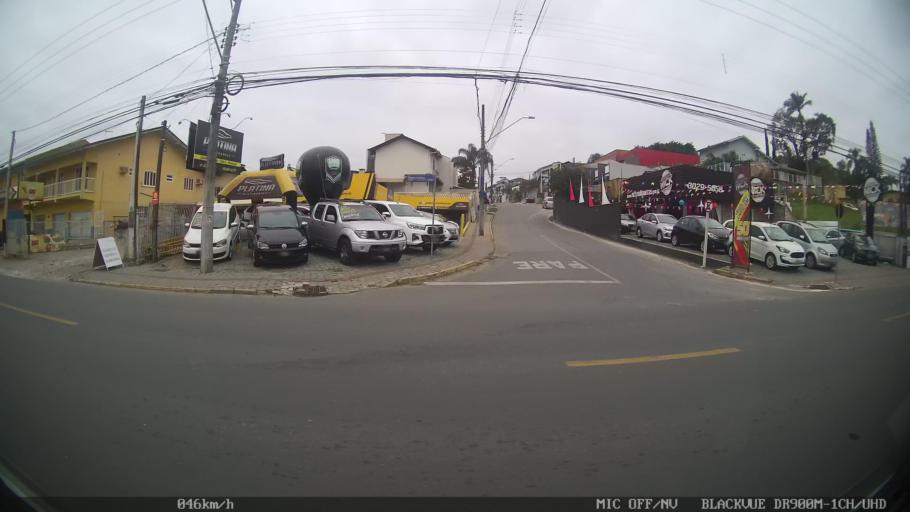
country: BR
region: Santa Catarina
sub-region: Joinville
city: Joinville
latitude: -26.3464
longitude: -48.8472
